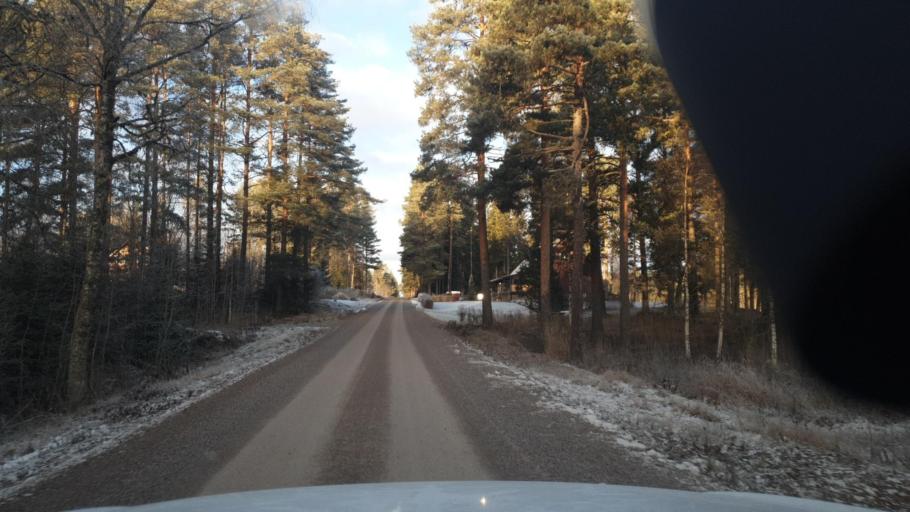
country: SE
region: Vaermland
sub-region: Eda Kommun
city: Charlottenberg
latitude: 60.0854
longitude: 12.5188
